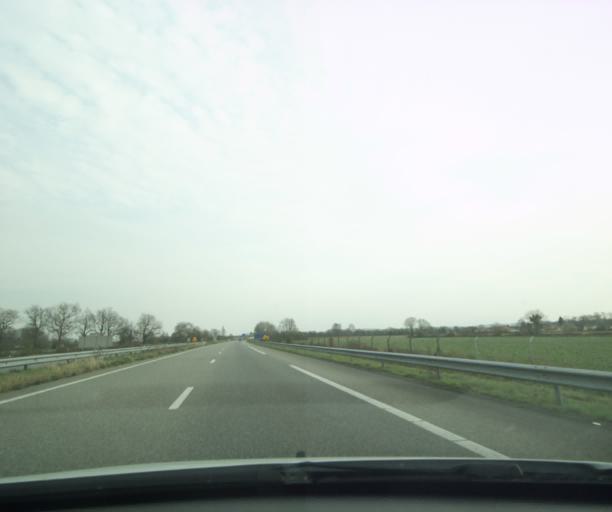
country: FR
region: Aquitaine
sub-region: Departement des Pyrenees-Atlantiques
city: Artix
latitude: 43.4055
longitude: -0.5577
